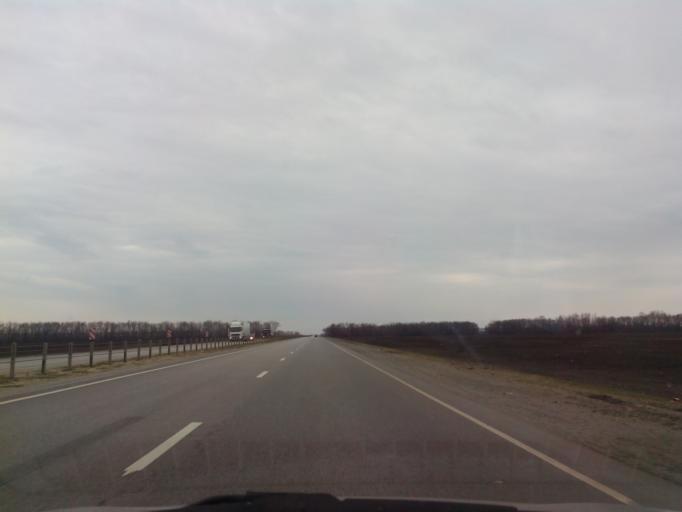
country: RU
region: Tambov
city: Zavoronezhskoye
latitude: 52.8930
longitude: 40.6903
